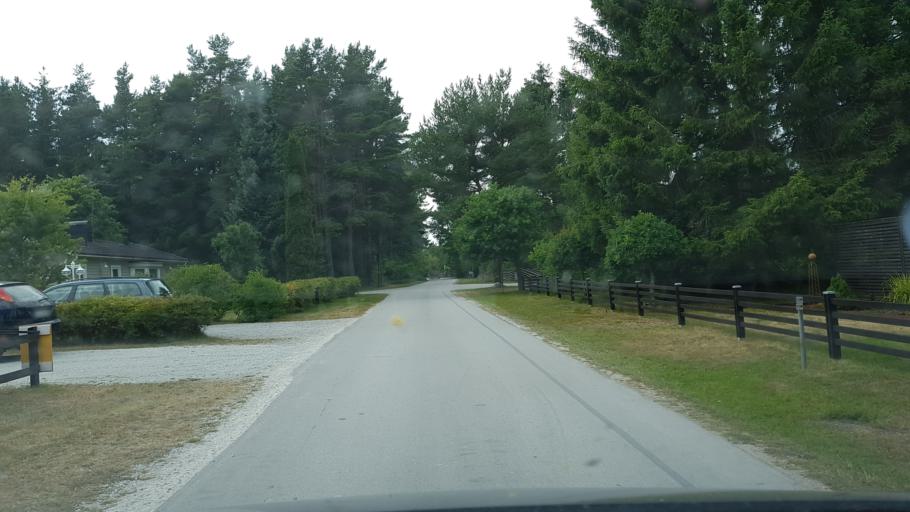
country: SE
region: Gotland
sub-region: Gotland
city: Hemse
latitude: 57.3383
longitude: 18.7134
